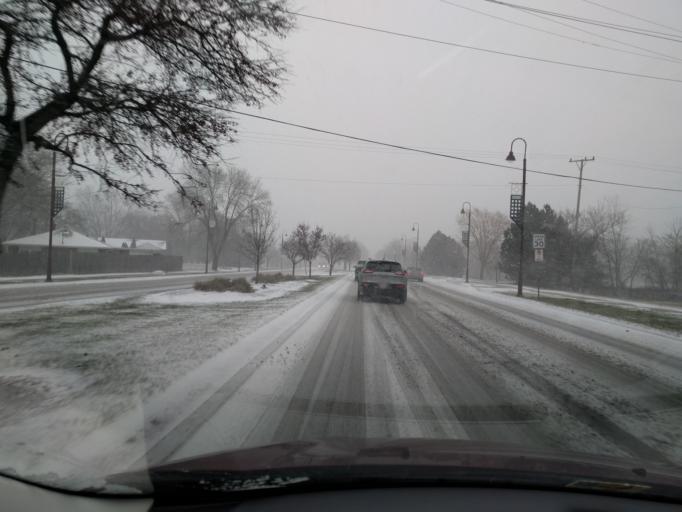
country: US
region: Wisconsin
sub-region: Milwaukee County
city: Glendale
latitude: 43.1190
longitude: -87.9425
